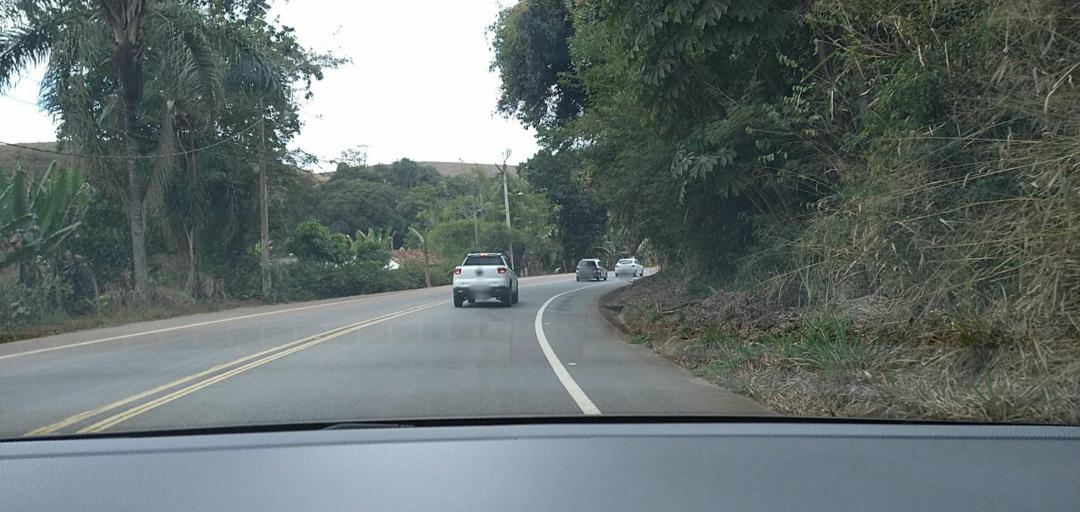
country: BR
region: Minas Gerais
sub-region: Ponte Nova
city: Ponte Nova
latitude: -20.5128
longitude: -42.8971
